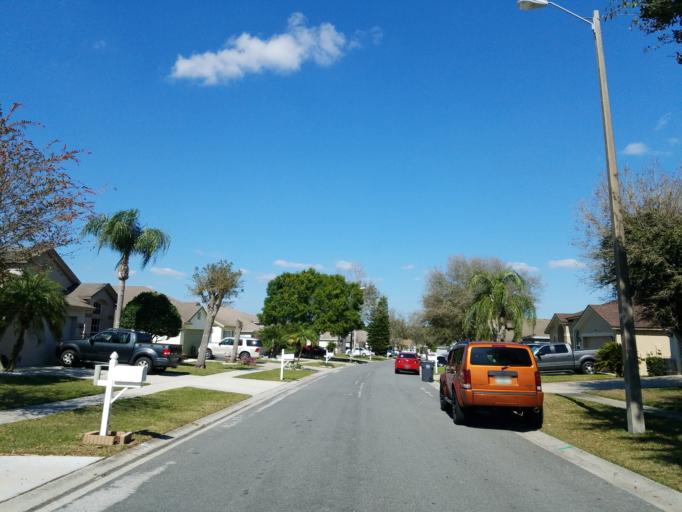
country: US
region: Florida
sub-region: Hillsborough County
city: Brandon
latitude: 27.9314
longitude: -82.2632
